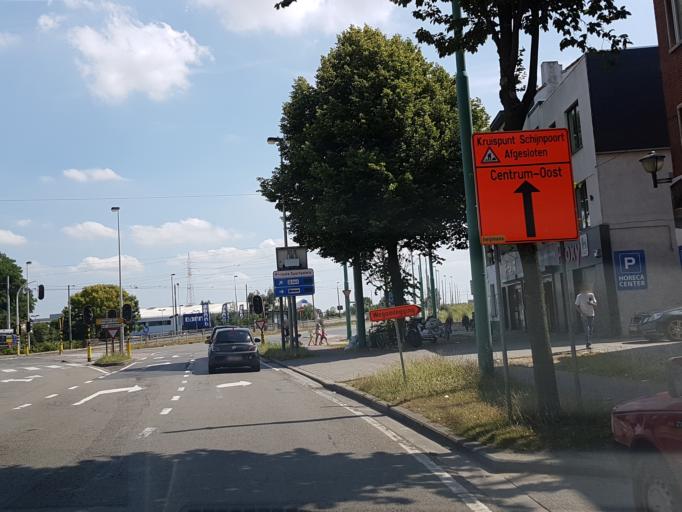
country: BE
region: Flanders
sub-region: Provincie Antwerpen
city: Antwerpen
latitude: 51.2387
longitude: 4.4399
